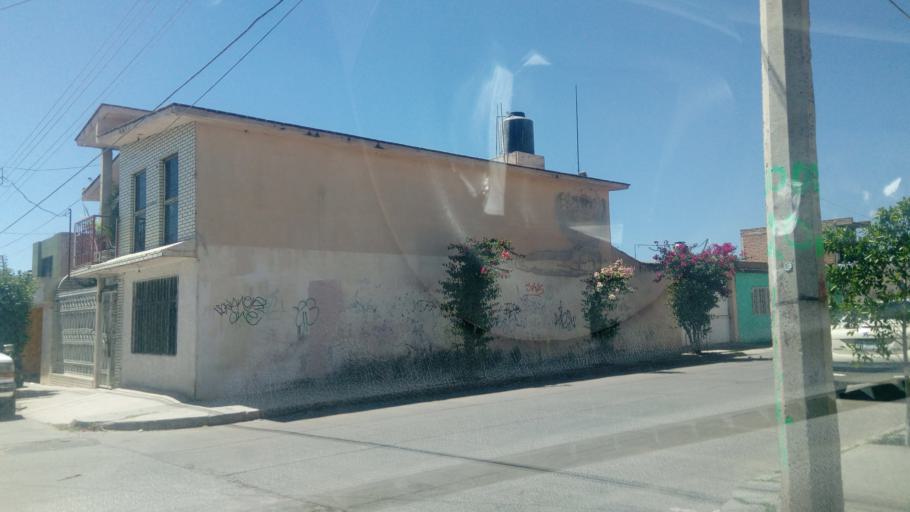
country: MX
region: Durango
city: Victoria de Durango
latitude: 24.0405
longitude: -104.6640
